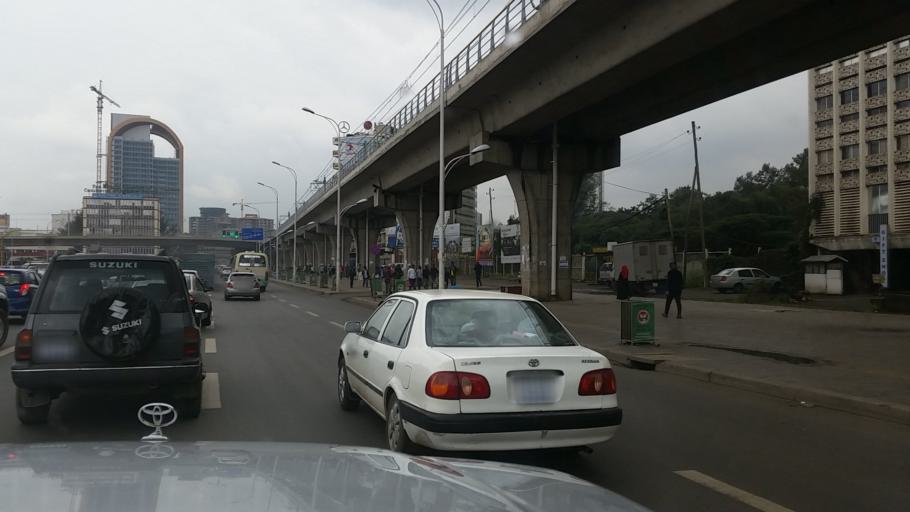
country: ET
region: Adis Abeba
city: Addis Ababa
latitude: 9.0112
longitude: 38.7614
